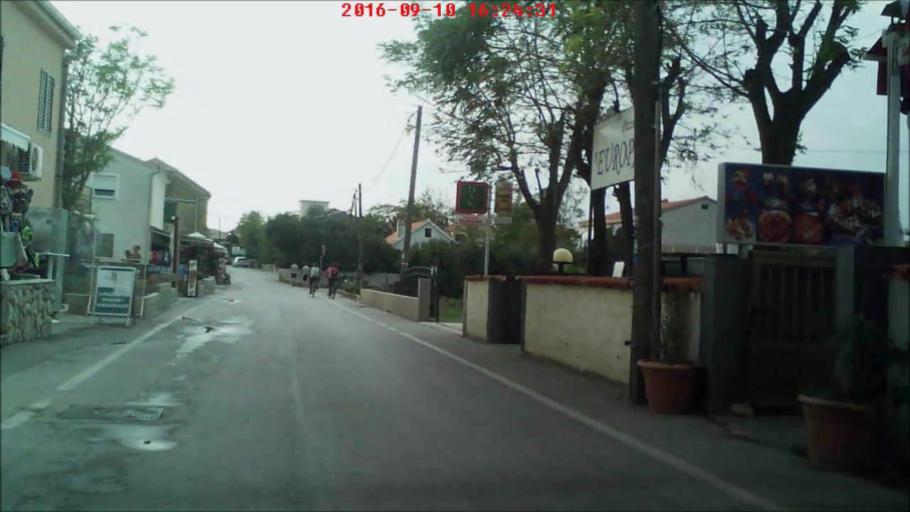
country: HR
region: Zadarska
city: Vir
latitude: 44.3009
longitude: 15.0854
